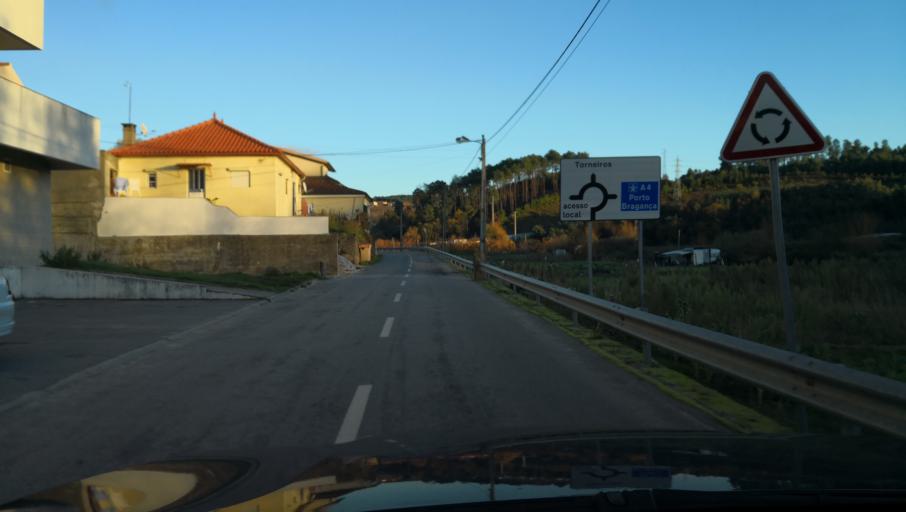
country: PT
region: Vila Real
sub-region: Vila Real
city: Vila Real
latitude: 41.2910
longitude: -7.7260
